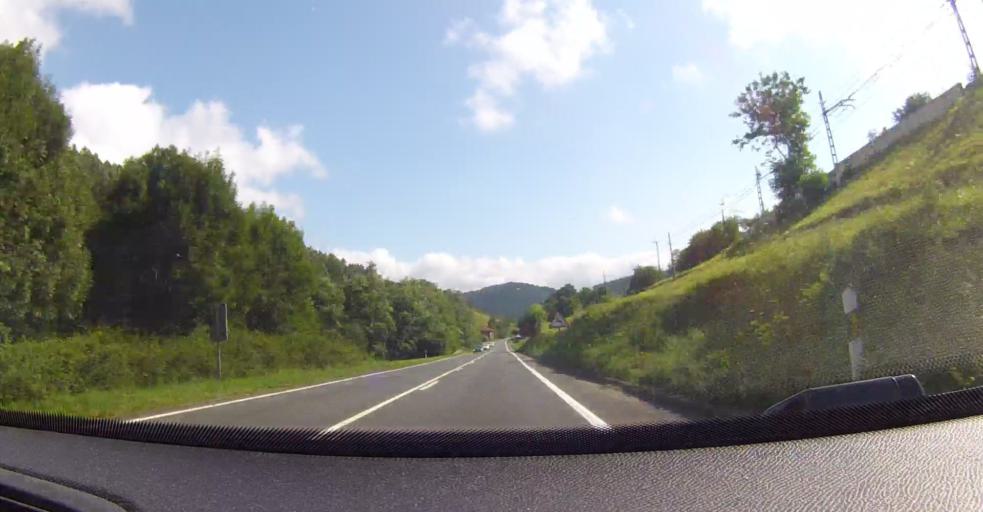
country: ES
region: Basque Country
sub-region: Bizkaia
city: Muxika
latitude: 43.2791
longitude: -2.6847
